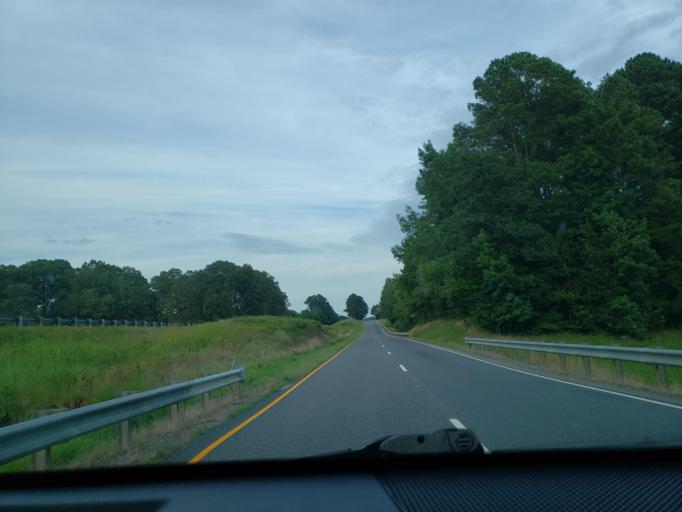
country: US
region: Virginia
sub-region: Brunswick County
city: Lawrenceville
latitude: 36.7227
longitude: -77.9478
